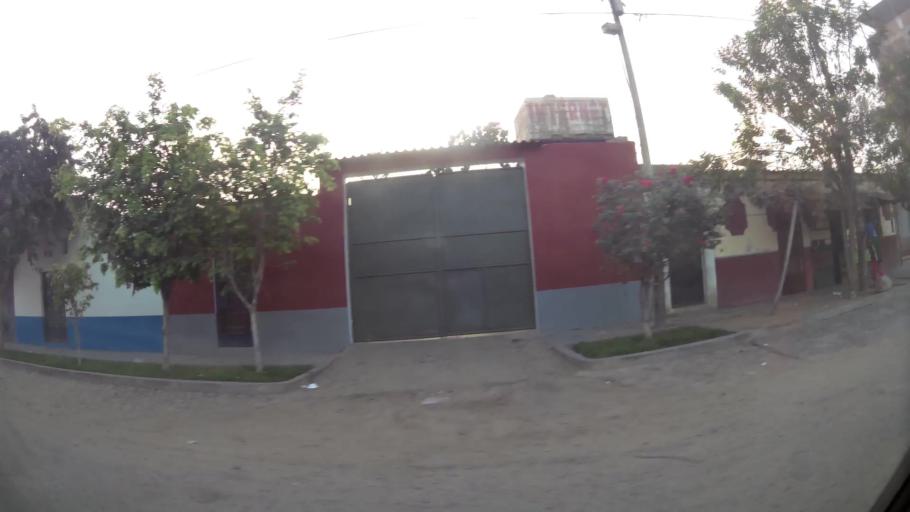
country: PE
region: La Libertad
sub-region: Provincia de Trujillo
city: El Porvenir
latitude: -8.0757
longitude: -78.9978
